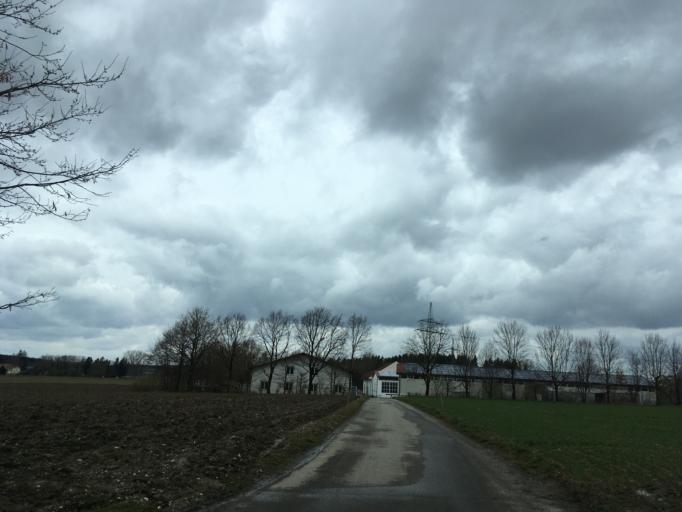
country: DE
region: Bavaria
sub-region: Upper Bavaria
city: Markt Schwaben
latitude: 48.1744
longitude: 11.8605
